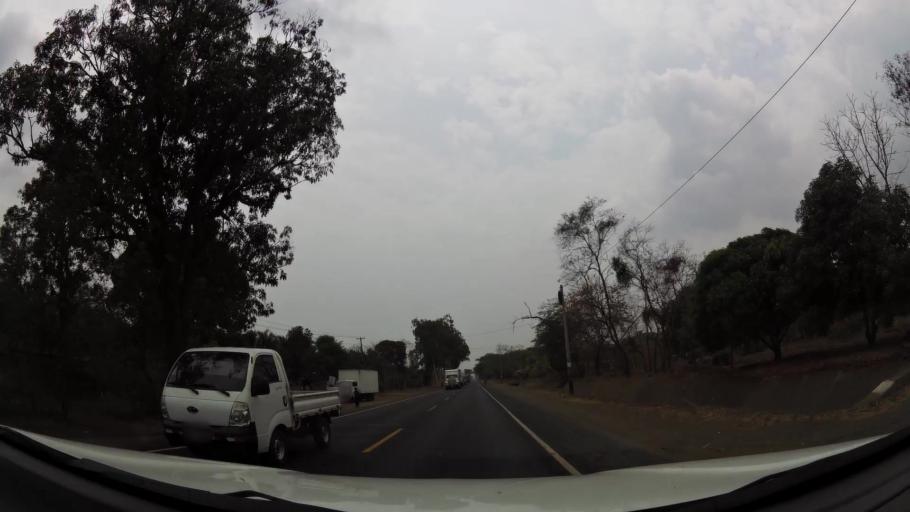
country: NI
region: Leon
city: Quezalguaque
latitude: 12.5376
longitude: -86.9060
